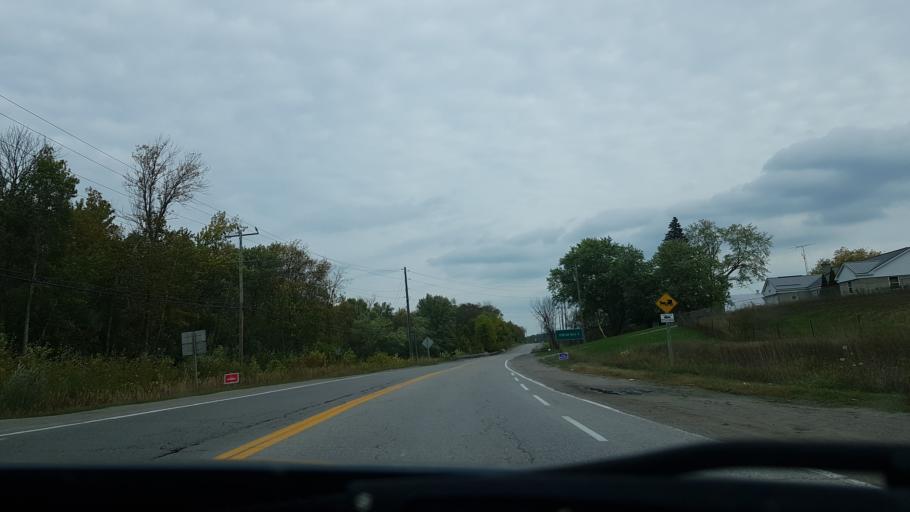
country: CA
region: Ontario
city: Omemee
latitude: 44.5217
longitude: -78.7760
